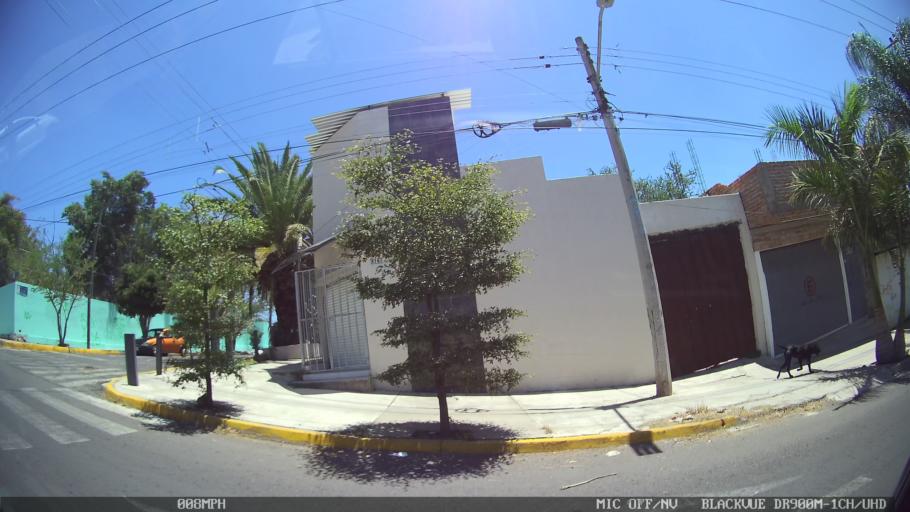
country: MX
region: Jalisco
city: Tlaquepaque
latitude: 20.6786
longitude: -103.2694
